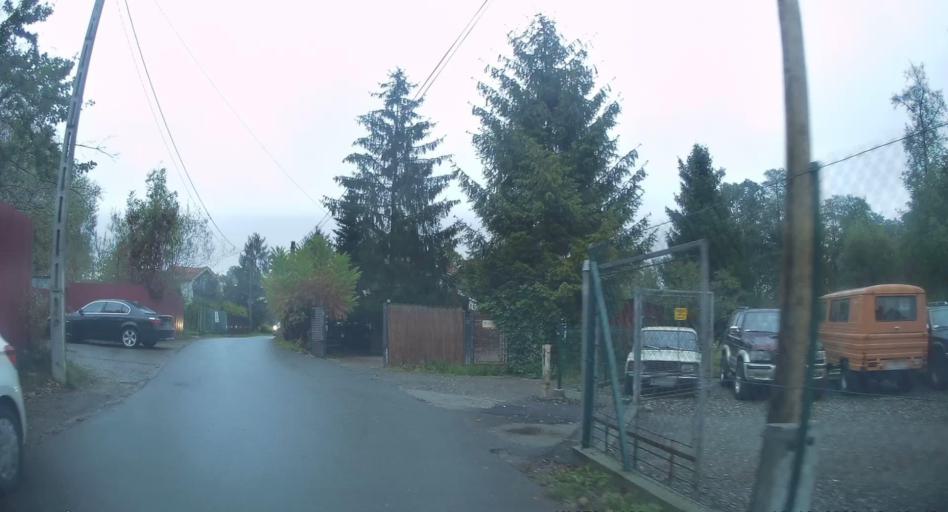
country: PL
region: Lesser Poland Voivodeship
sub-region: Powiat krakowski
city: Ochojno
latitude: 50.0106
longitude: 19.9805
